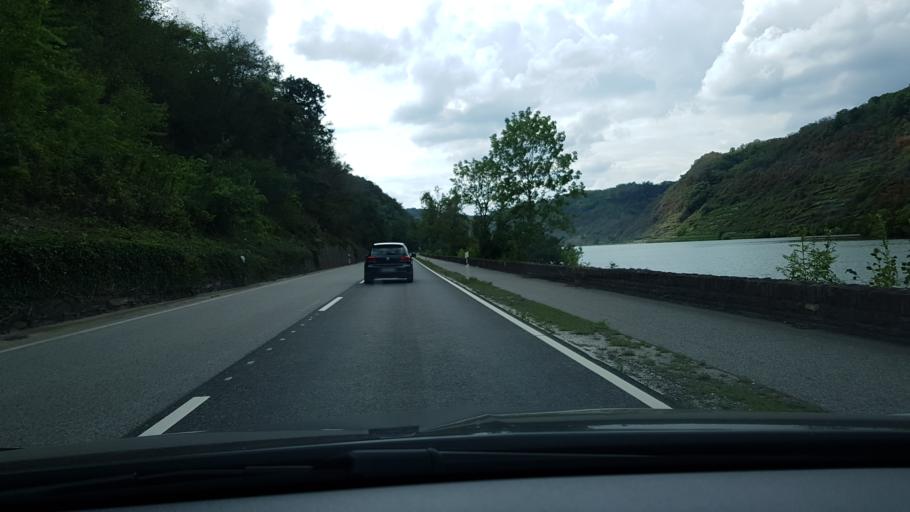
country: DE
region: Rheinland-Pfalz
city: Lehmen
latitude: 50.2697
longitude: 7.4574
